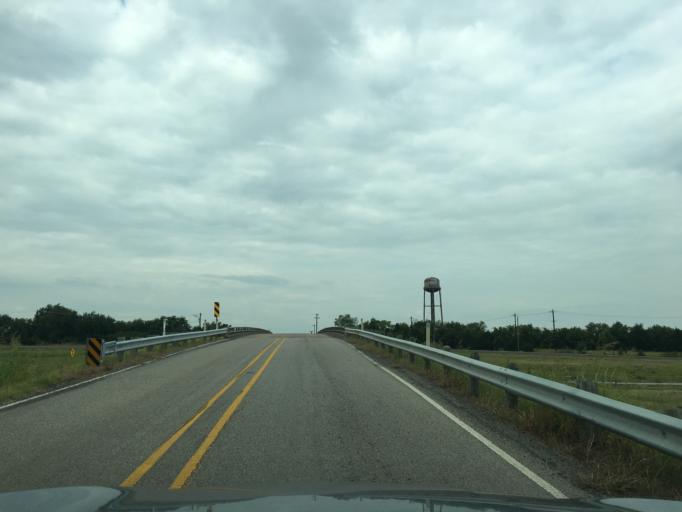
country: US
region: Texas
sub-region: Grayson County
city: Van Alstyne
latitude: 33.3819
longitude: -96.5799
